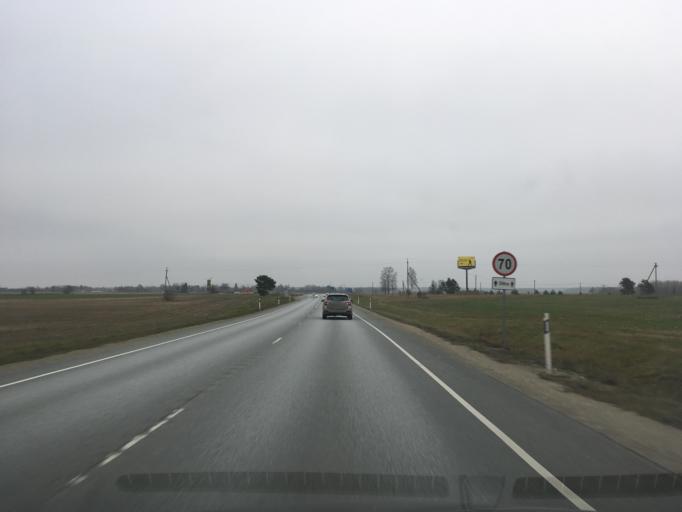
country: EE
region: Ida-Virumaa
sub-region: Puessi linn
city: Pussi
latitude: 59.4044
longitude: 27.0679
